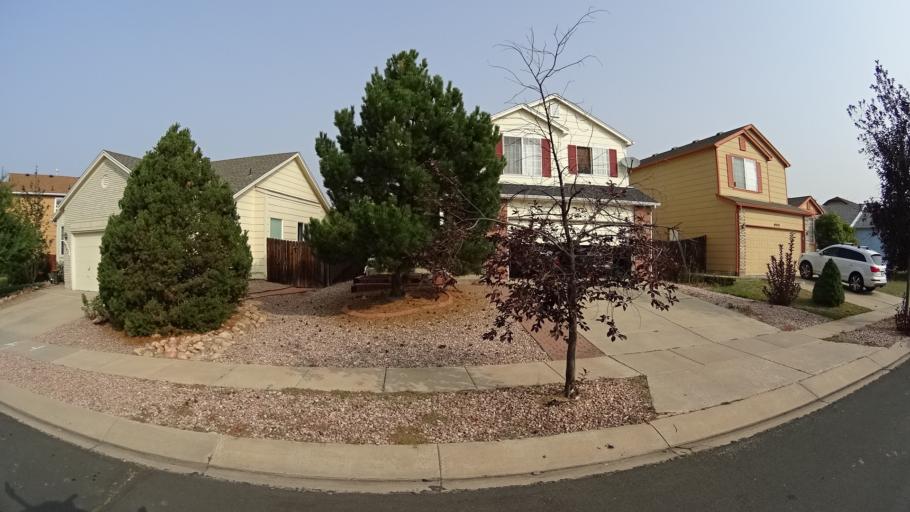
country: US
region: Colorado
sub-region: El Paso County
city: Cimarron Hills
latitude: 38.9344
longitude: -104.7363
